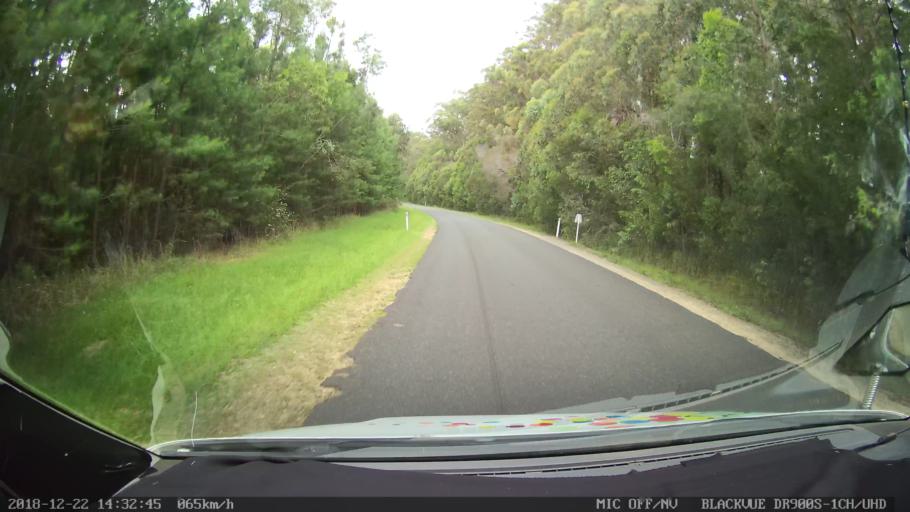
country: AU
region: New South Wales
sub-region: Bellingen
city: Dorrigo
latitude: -30.1067
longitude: 152.6245
